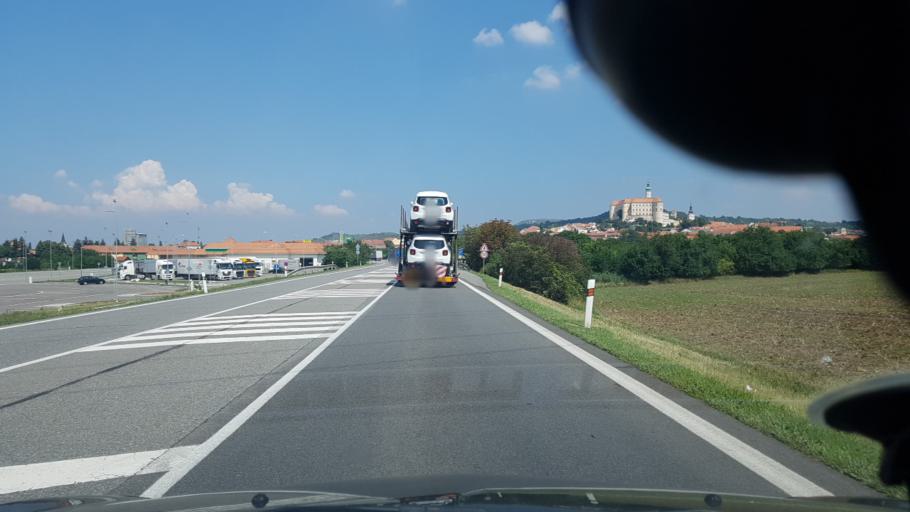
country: CZ
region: South Moravian
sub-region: Okres Breclav
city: Mikulov
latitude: 48.7964
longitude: 16.6334
